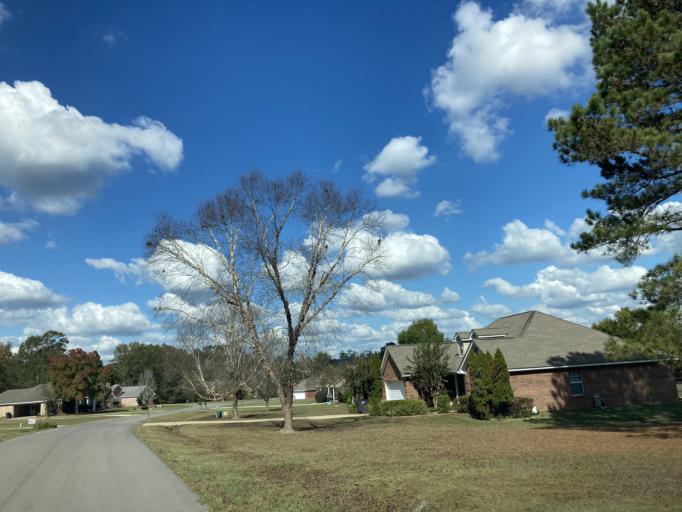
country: US
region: Mississippi
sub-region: Lamar County
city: West Hattiesburg
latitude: 31.2706
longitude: -89.3845
